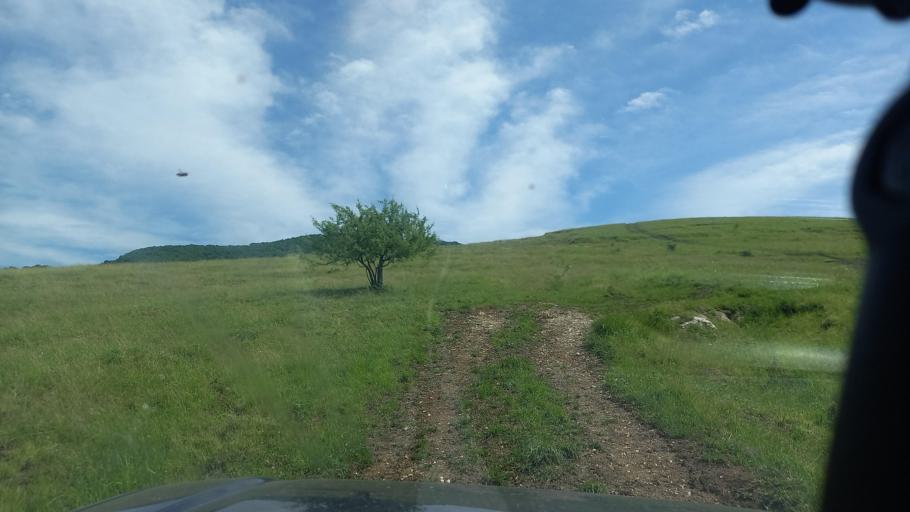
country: RU
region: Karachayevo-Cherkesiya
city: Kurdzhinovo
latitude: 44.1427
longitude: 41.0586
